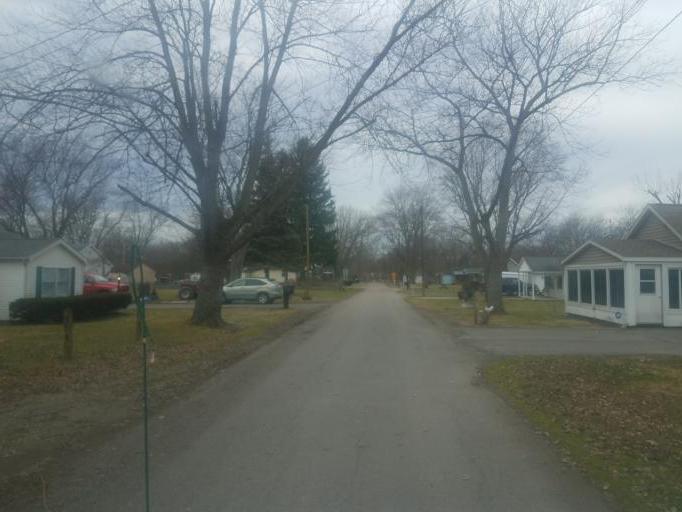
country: US
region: Ohio
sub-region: Marion County
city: Marion
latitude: 40.5970
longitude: -83.1082
